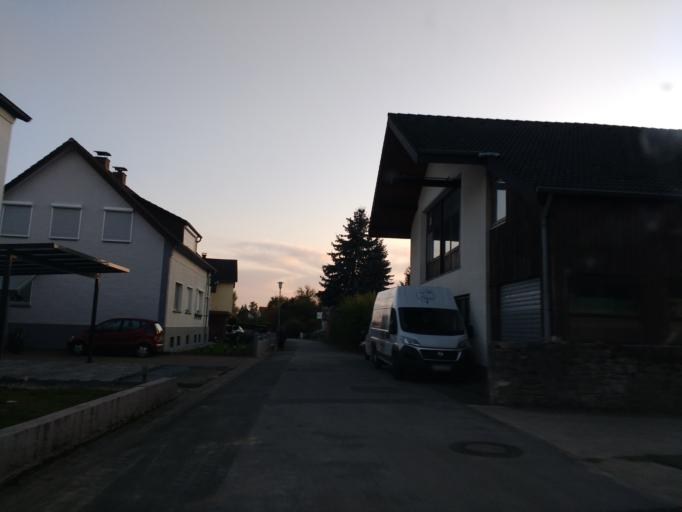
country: DE
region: North Rhine-Westphalia
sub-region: Regierungsbezirk Detmold
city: Schlangen
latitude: 51.8076
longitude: 8.8424
